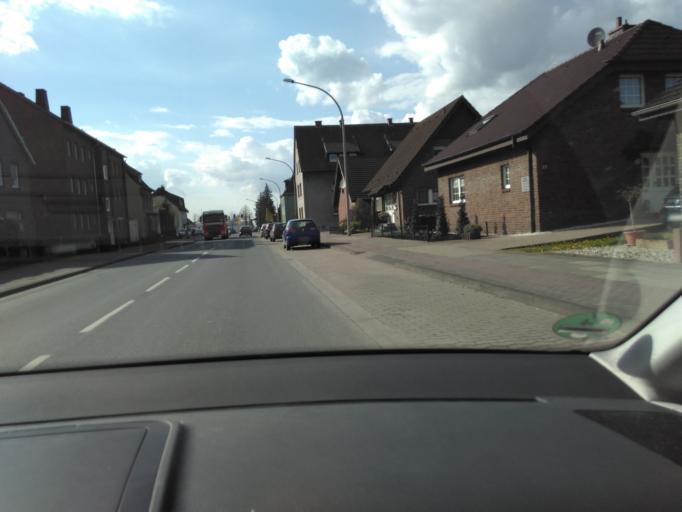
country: DE
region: North Rhine-Westphalia
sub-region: Regierungsbezirk Munster
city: Beckum
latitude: 51.7640
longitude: 8.0455
